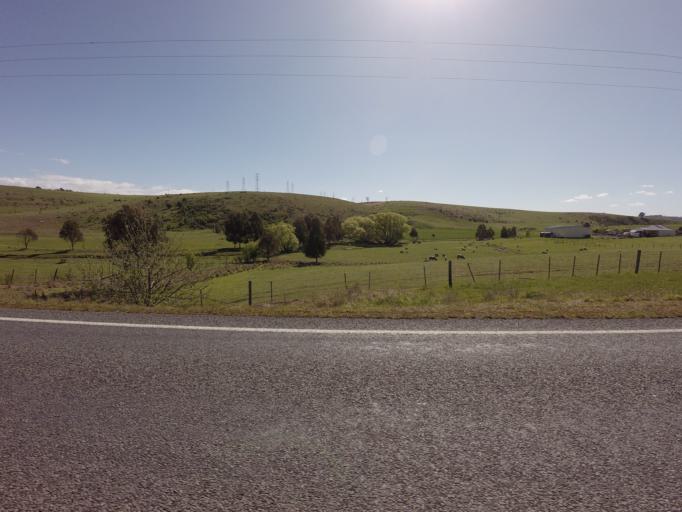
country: AU
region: Tasmania
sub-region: Derwent Valley
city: New Norfolk
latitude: -42.6614
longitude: 146.9348
